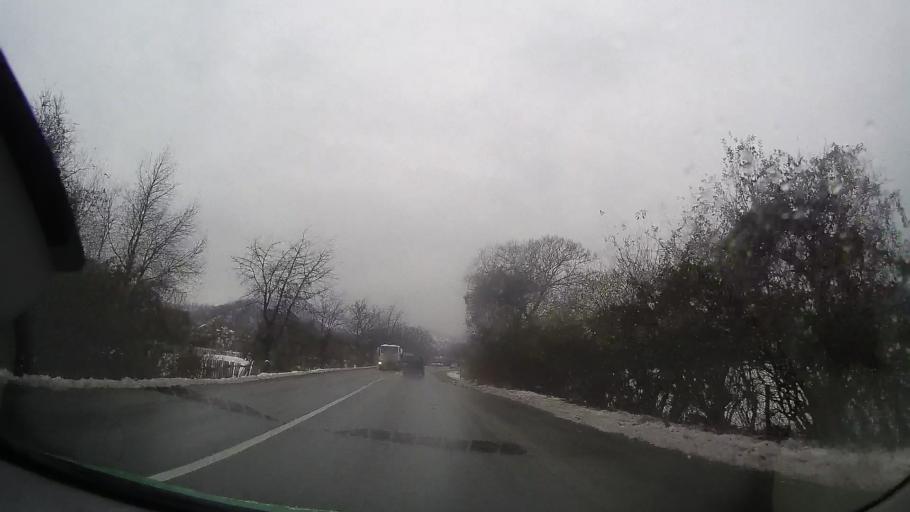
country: RO
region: Neamt
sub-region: Comuna Pangarati
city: Stejaru
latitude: 46.9187
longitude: 26.1889
